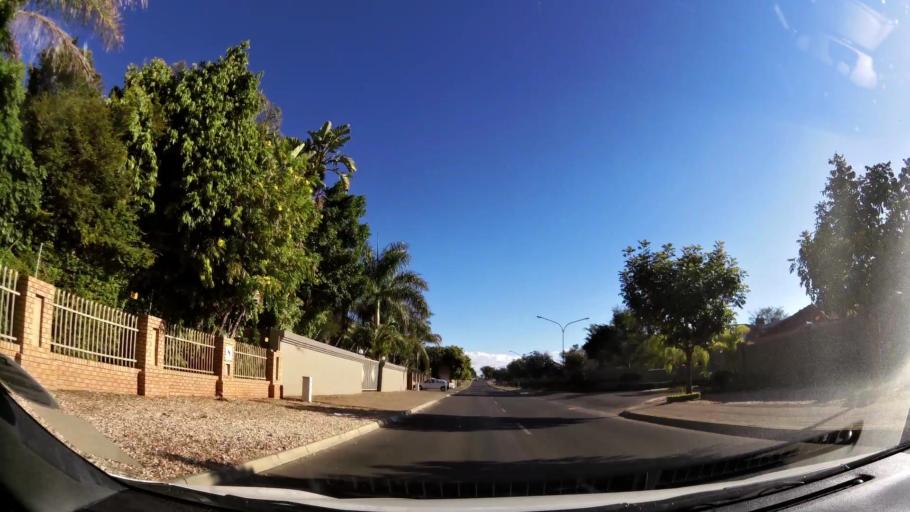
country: ZA
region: Limpopo
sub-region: Capricorn District Municipality
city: Polokwane
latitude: -23.8795
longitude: 29.4914
